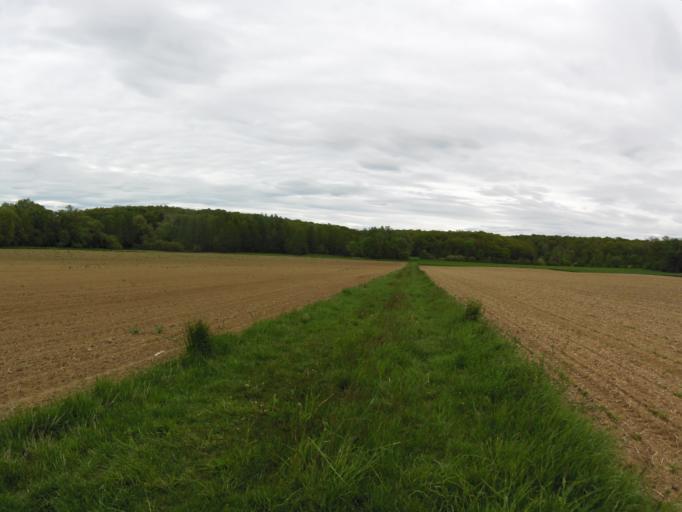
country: DE
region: Bavaria
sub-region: Regierungsbezirk Unterfranken
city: Kurnach
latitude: 49.8456
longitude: 10.0618
